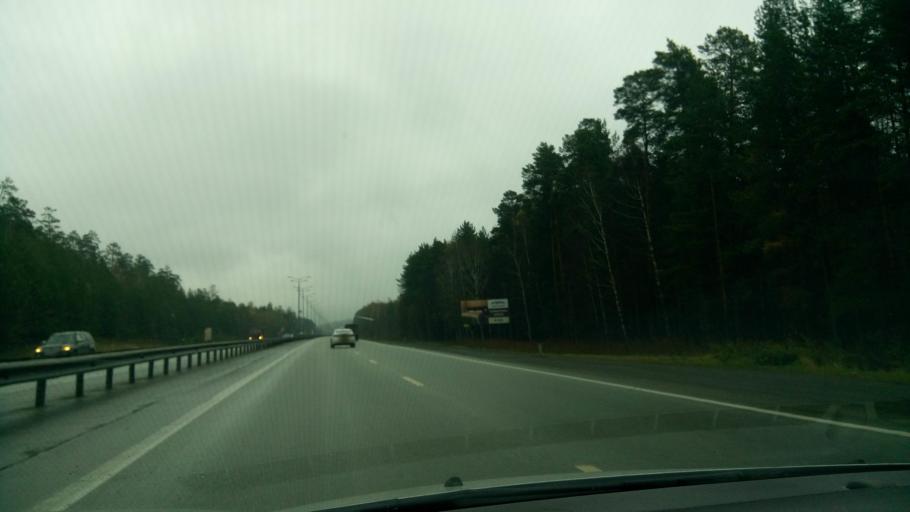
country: RU
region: Sverdlovsk
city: Severka
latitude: 56.8414
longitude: 60.2560
